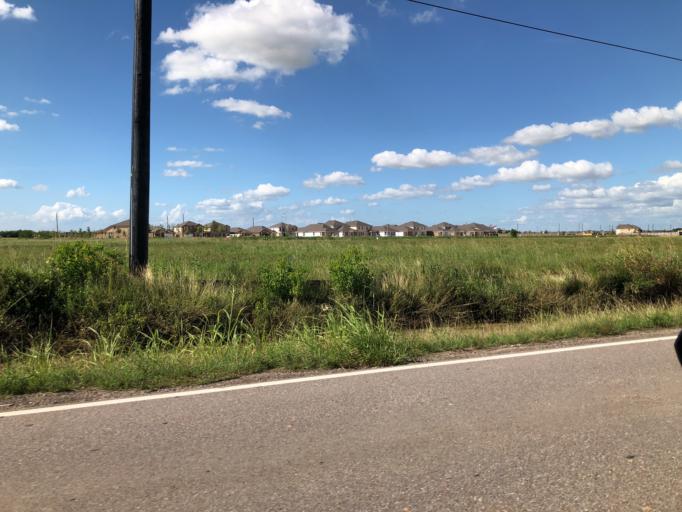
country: US
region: Texas
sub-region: Harris County
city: Katy
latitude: 29.8315
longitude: -95.7965
